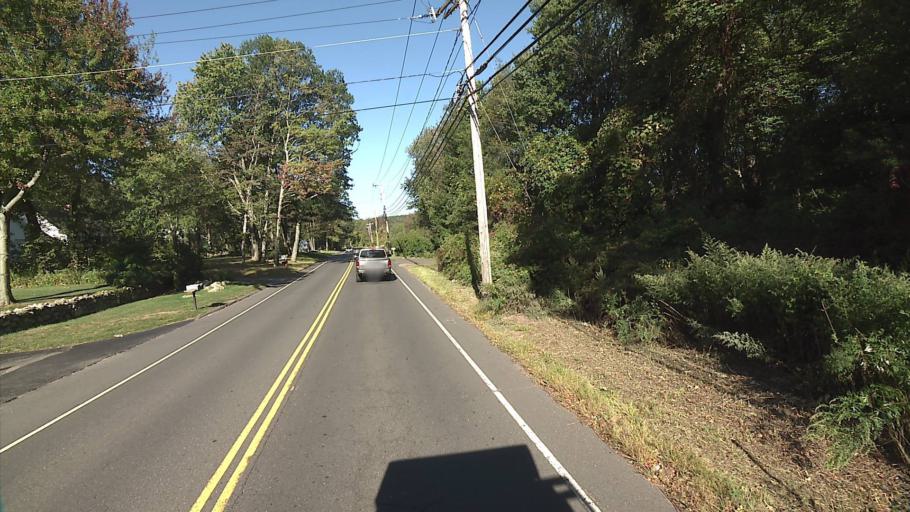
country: US
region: Connecticut
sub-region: New Haven County
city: Prospect
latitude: 41.4993
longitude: -72.9616
